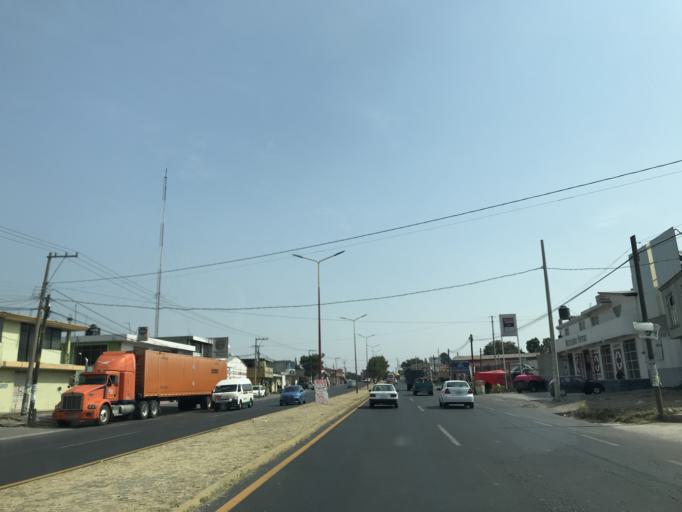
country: MX
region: Tlaxcala
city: La Magdalena Tlaltelulco
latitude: 19.2679
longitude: -98.1982
